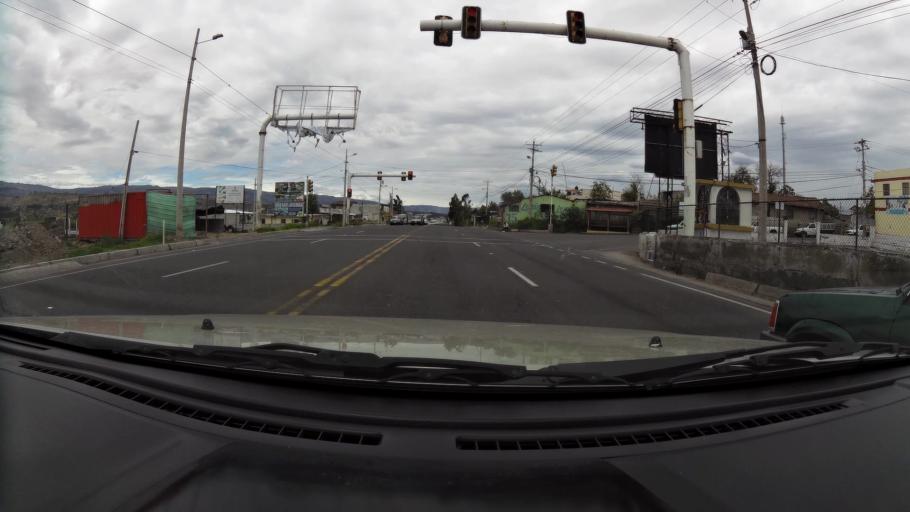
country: EC
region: Cotopaxi
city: Latacunga
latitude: -0.9762
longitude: -78.6069
